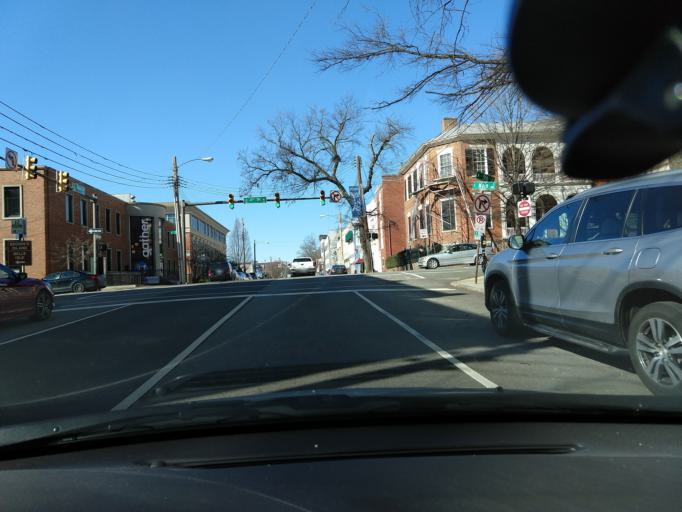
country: US
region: Virginia
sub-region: City of Richmond
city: Richmond
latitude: 37.5403
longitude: -77.4396
